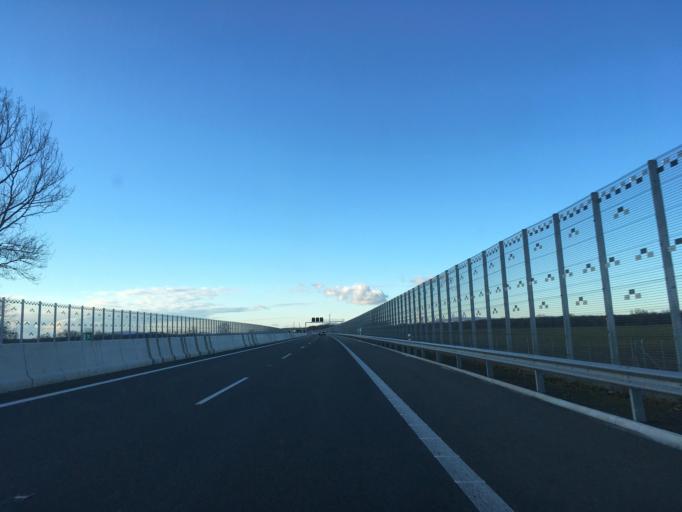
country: SK
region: Bratislavsky
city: Dunajska Luzna
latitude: 48.0782
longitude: 17.2402
